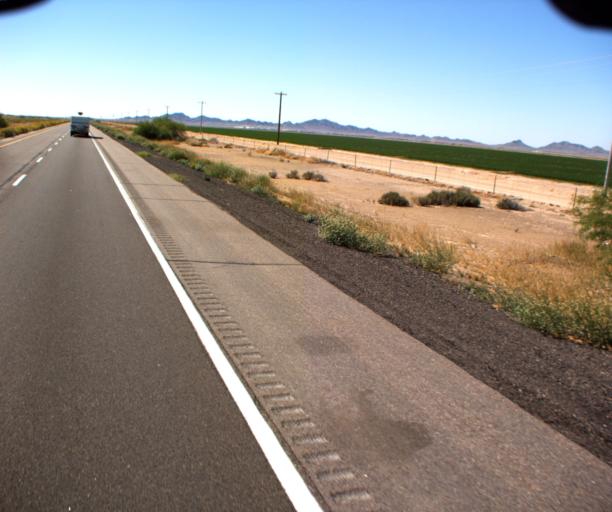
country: US
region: Arizona
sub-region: Maricopa County
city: Gila Bend
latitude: 32.9161
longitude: -112.9258
